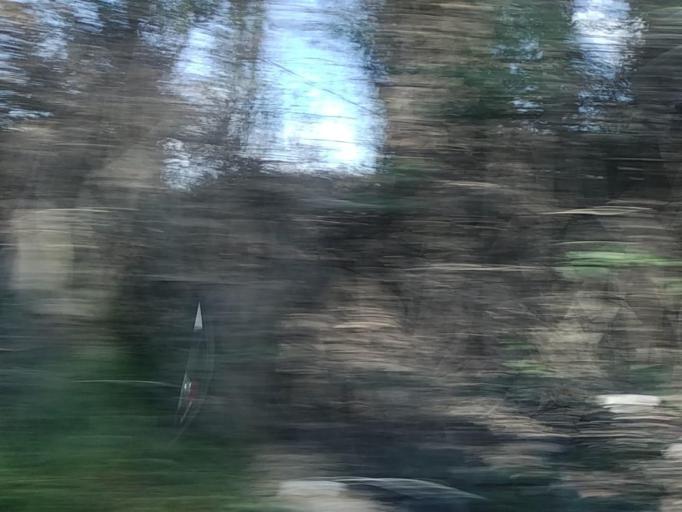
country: CL
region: Santiago Metropolitan
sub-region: Provincia de Chacabuco
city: Chicureo Abajo
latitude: -33.3107
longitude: -70.7168
